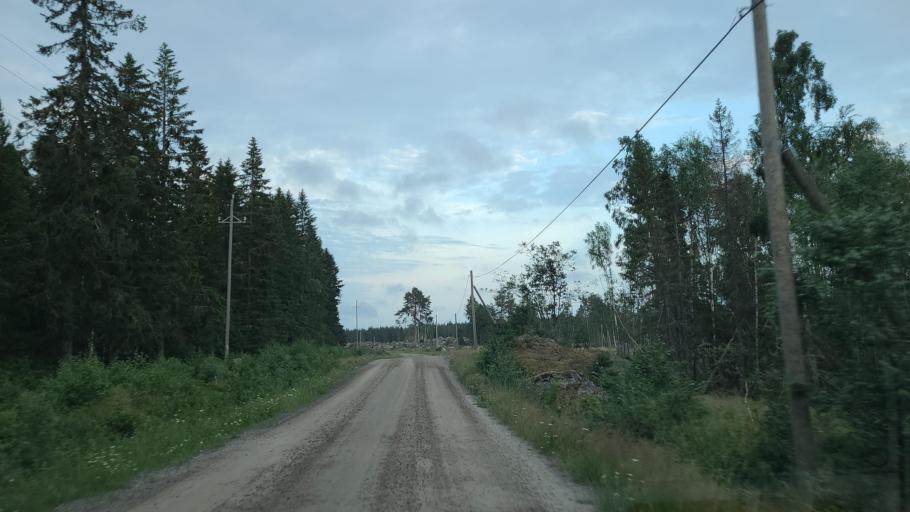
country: FI
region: Ostrobothnia
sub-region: Vaasa
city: Replot
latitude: 63.3202
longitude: 21.1458
